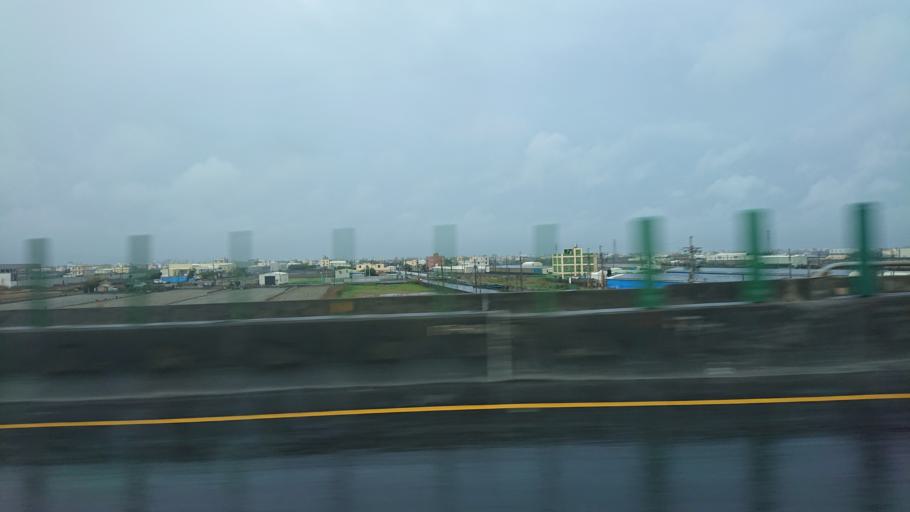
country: TW
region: Taiwan
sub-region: Changhua
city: Chang-hua
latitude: 24.1340
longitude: 120.4406
